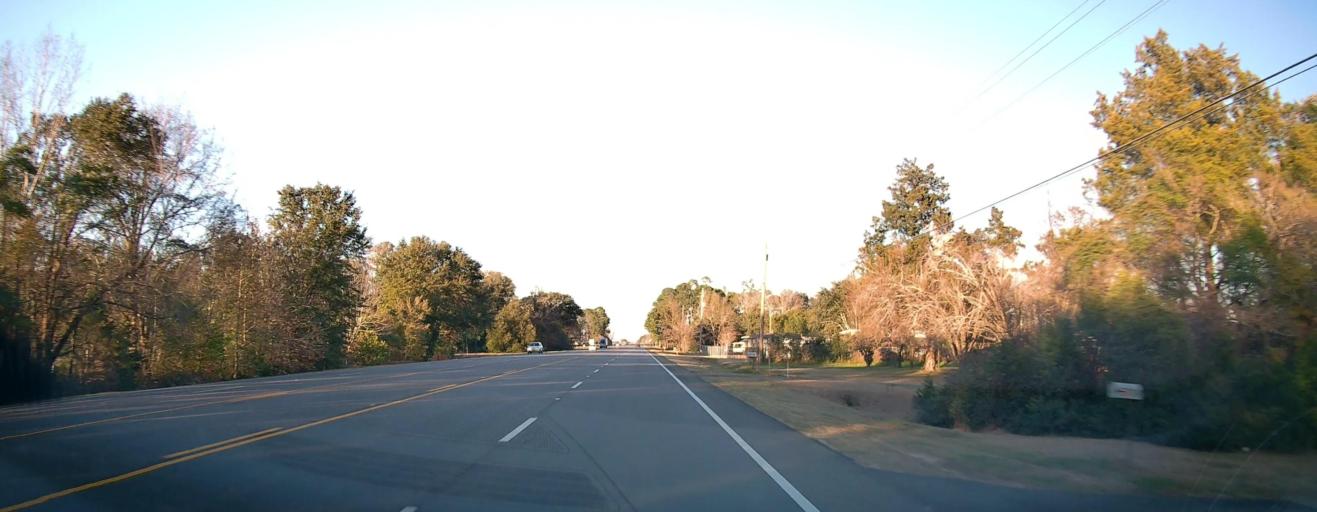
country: US
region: Georgia
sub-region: Dougherty County
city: Albany
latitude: 31.5162
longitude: -84.1992
